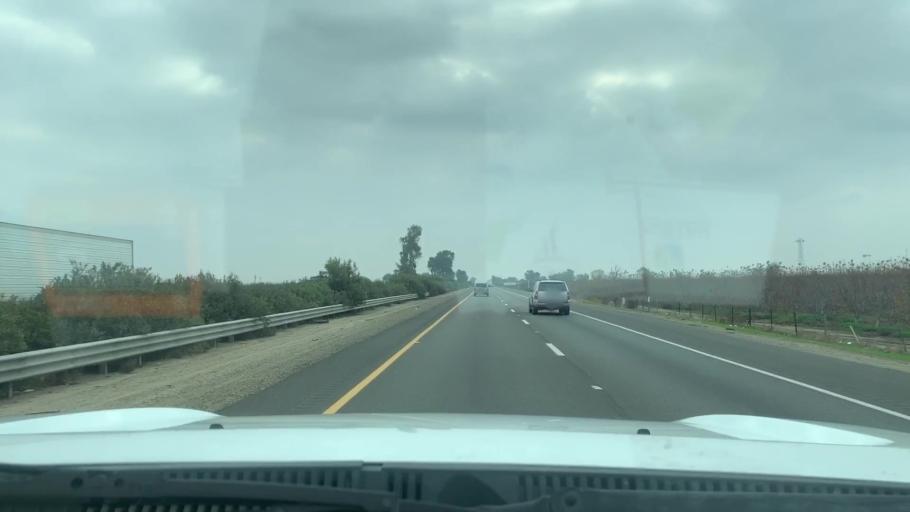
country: US
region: California
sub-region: Tulare County
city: Tipton
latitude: 36.1180
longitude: -119.3244
